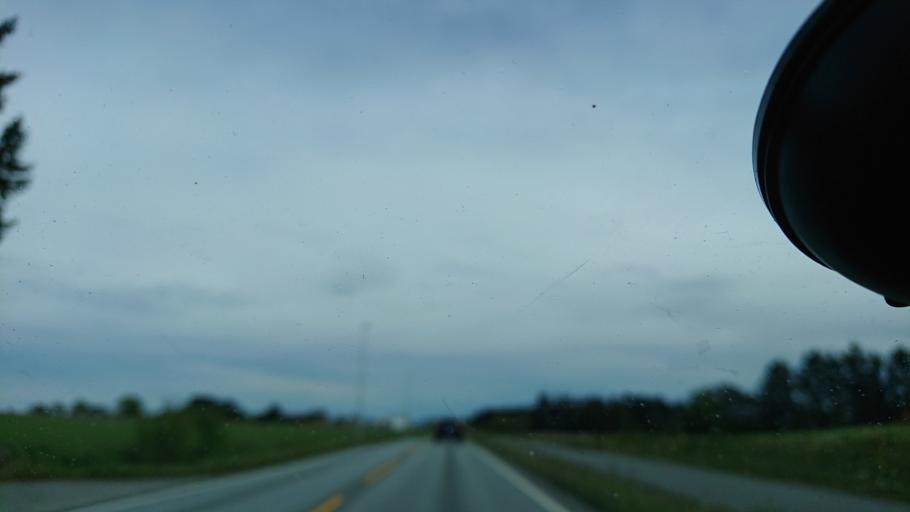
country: NO
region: Rogaland
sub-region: Sola
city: Tananger
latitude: 58.9423
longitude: 5.6022
